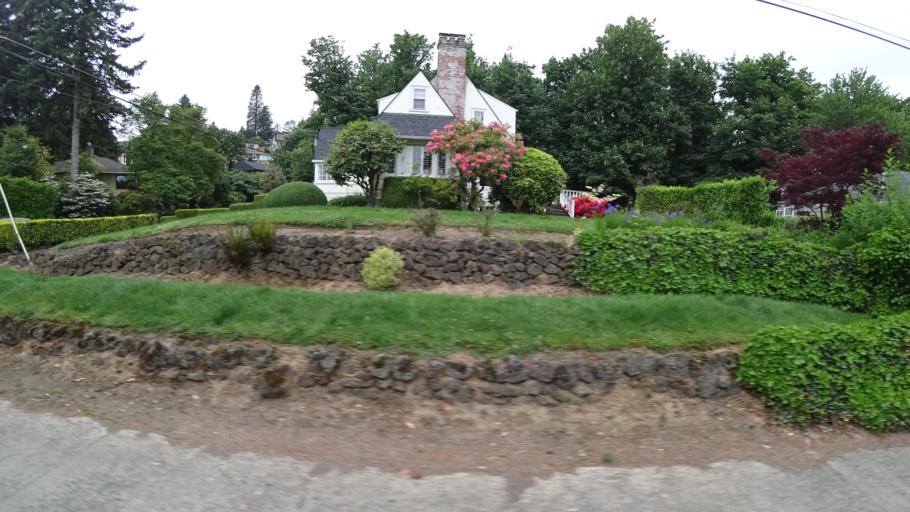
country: US
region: Oregon
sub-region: Multnomah County
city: Portland
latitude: 45.4845
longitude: -122.6873
